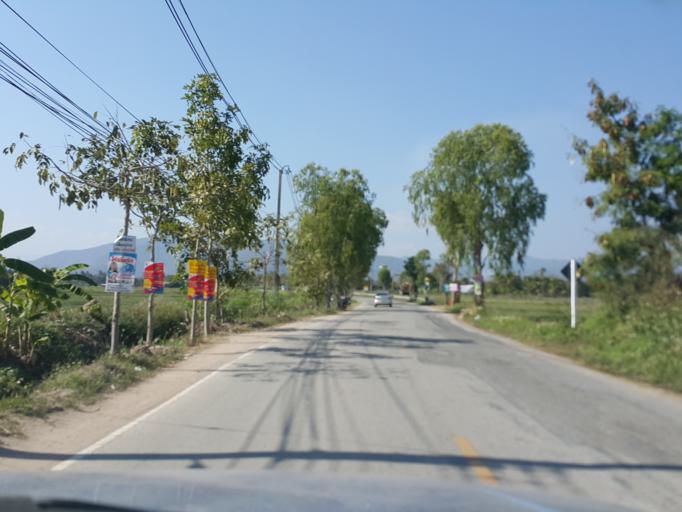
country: TH
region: Chiang Mai
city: Mae Wang
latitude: 18.6009
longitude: 98.8011
